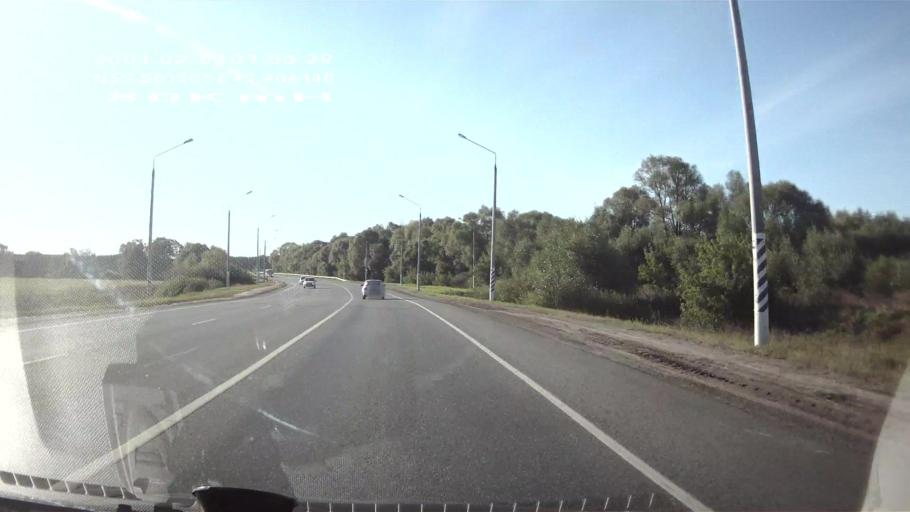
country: RU
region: Chuvashia
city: Shikhazany
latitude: 55.5611
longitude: 47.4044
